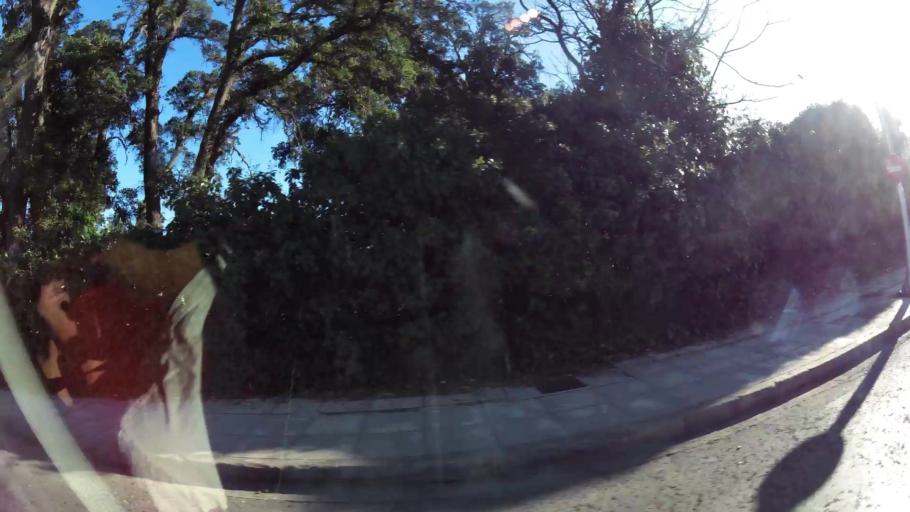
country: GR
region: Attica
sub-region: Nomarchia Athinas
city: Marousi
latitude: 38.0579
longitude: 23.8088
